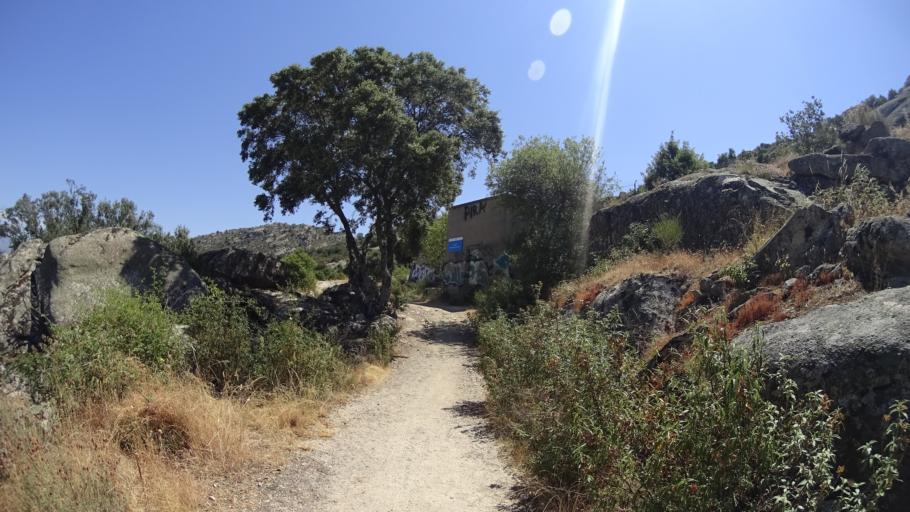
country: ES
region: Madrid
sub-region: Provincia de Madrid
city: Moralzarzal
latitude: 40.6424
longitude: -3.9636
